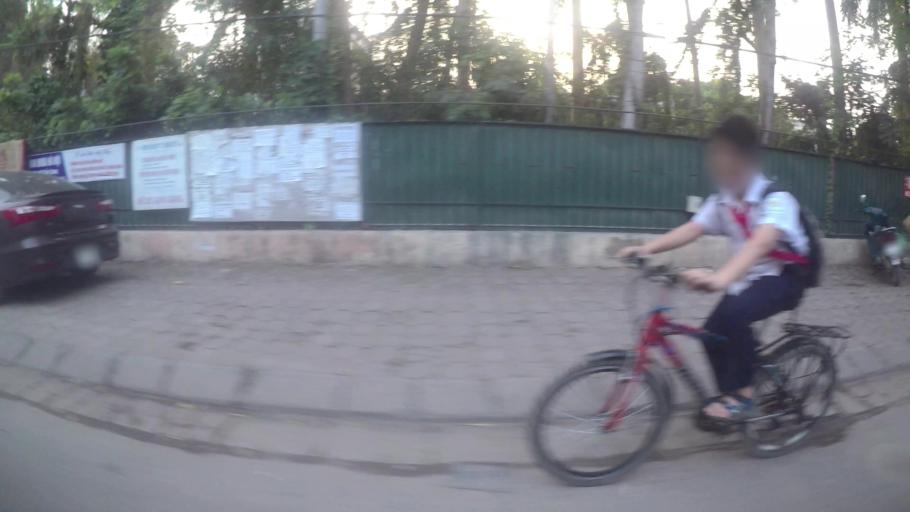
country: VN
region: Ha Noi
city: Cau Giay
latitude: 21.0490
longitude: 105.7899
